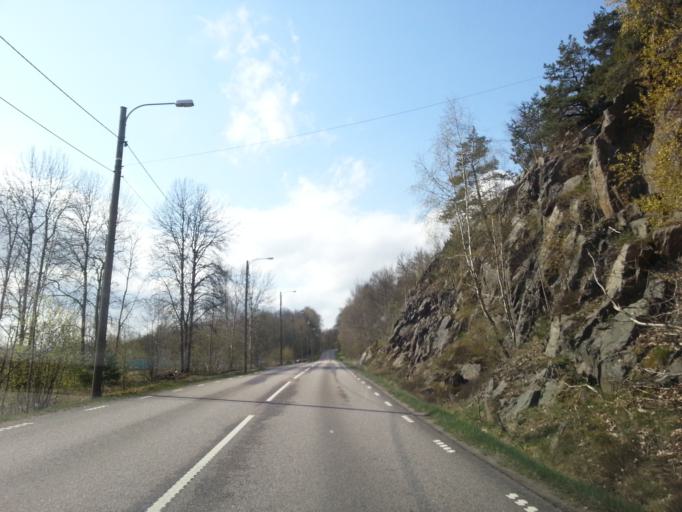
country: SE
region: Vaestra Goetaland
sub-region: Ale Kommun
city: Surte
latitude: 57.8154
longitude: 12.0006
